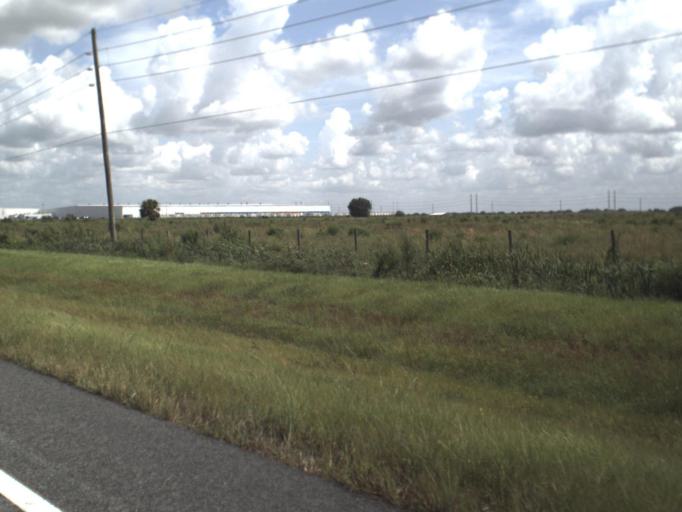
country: US
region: Florida
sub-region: Charlotte County
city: Harbour Heights
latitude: 27.0308
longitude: -81.9583
